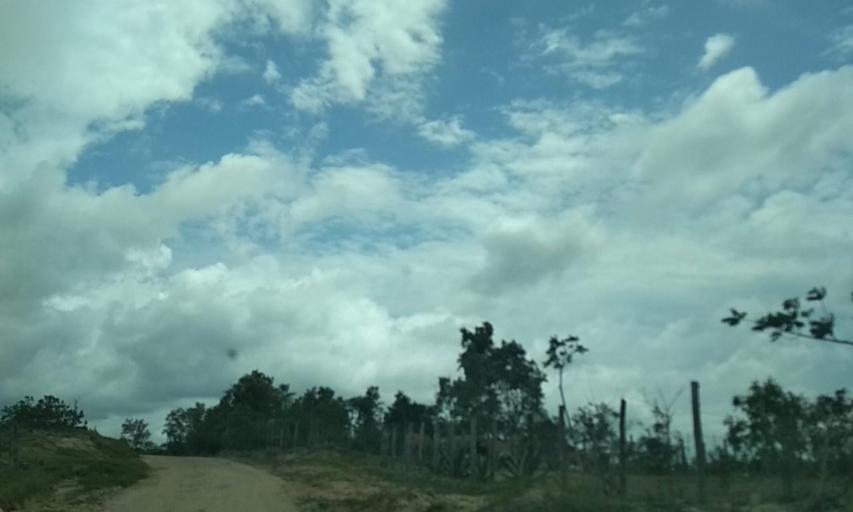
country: MX
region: Veracruz
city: Las Choapas
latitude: 17.9008
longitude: -94.1208
